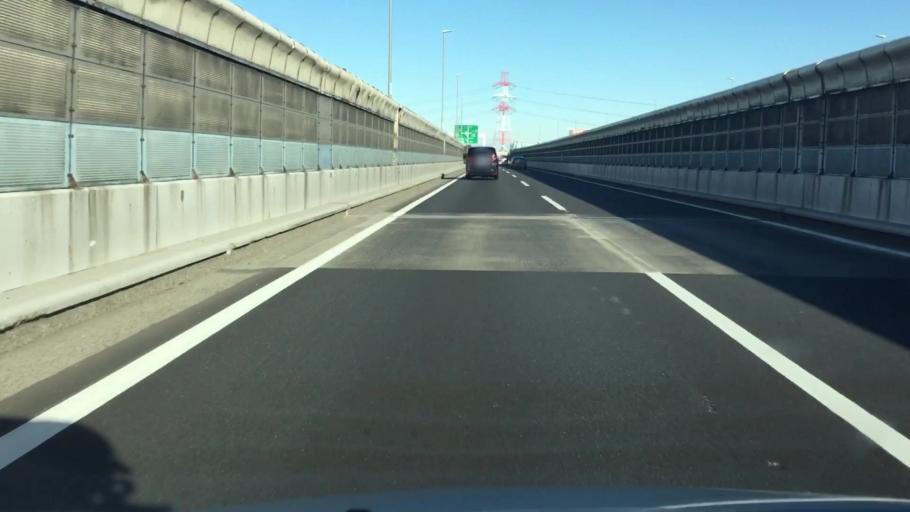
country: JP
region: Saitama
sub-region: Kawaguchi-shi
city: Hatogaya-honcho
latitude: 35.8343
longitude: 139.7559
